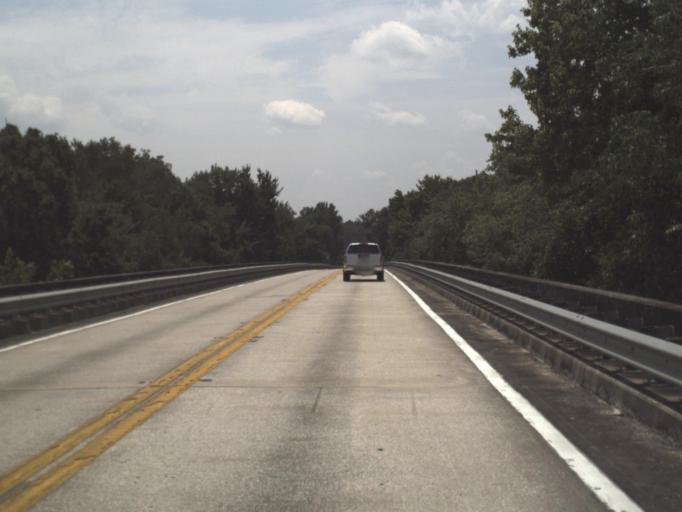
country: US
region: Florida
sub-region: Putnam County
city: Palatka
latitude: 29.4787
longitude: -81.7403
